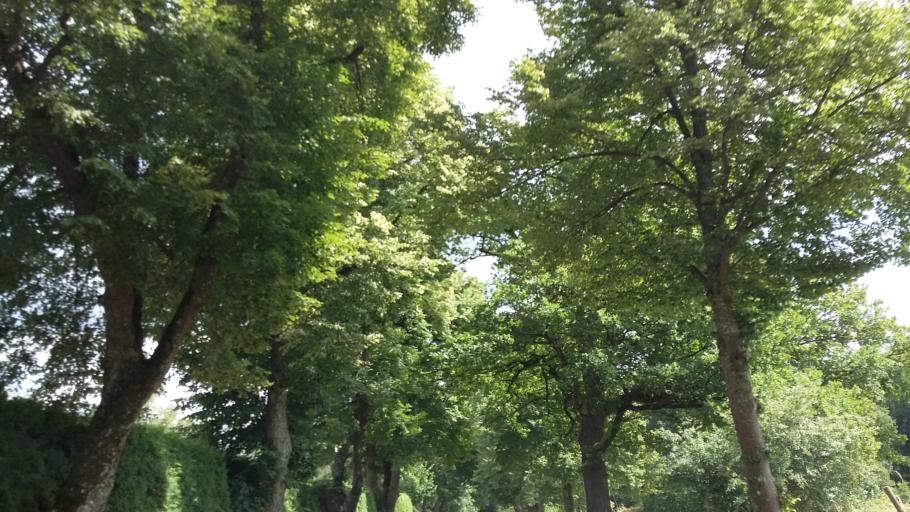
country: DE
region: Bavaria
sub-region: Upper Bavaria
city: Planegg
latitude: 48.0893
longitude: 11.4115
